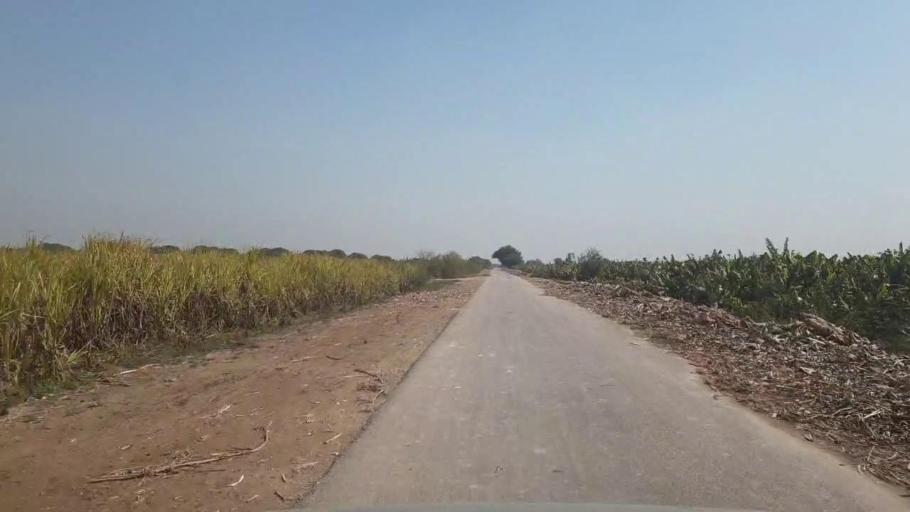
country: PK
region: Sindh
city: Chambar
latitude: 25.2422
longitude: 68.8548
